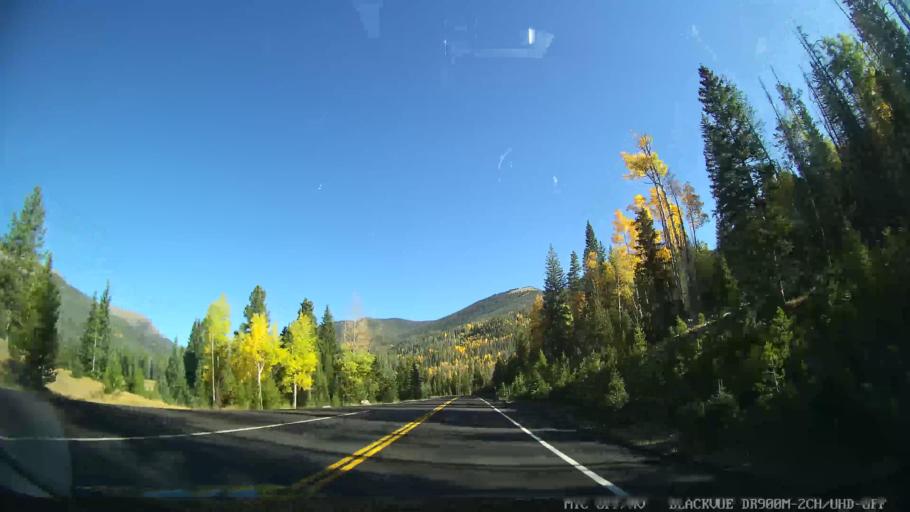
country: US
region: Colorado
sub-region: Grand County
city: Granby
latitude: 40.3923
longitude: -105.8458
